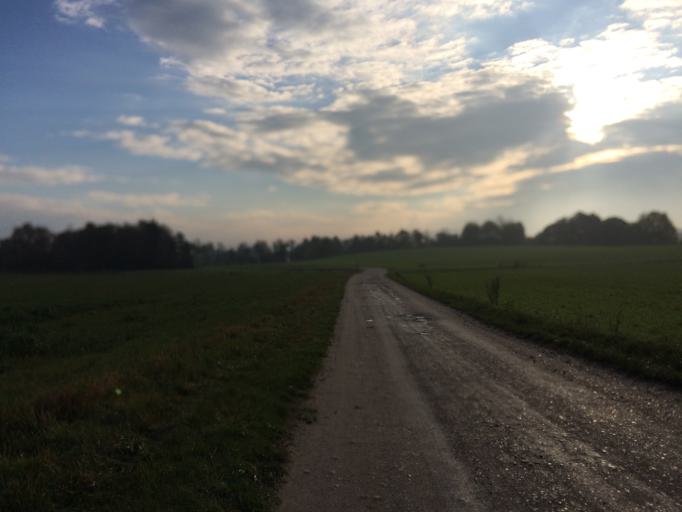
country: DK
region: Zealand
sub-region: Ringsted Kommune
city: Ringsted
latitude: 55.4852
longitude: 11.7419
